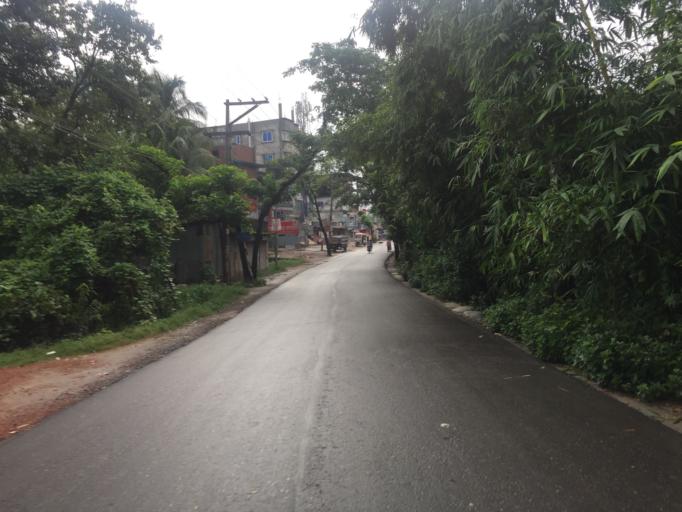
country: BD
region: Dhaka
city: Narayanganj
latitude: 23.5497
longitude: 90.4940
